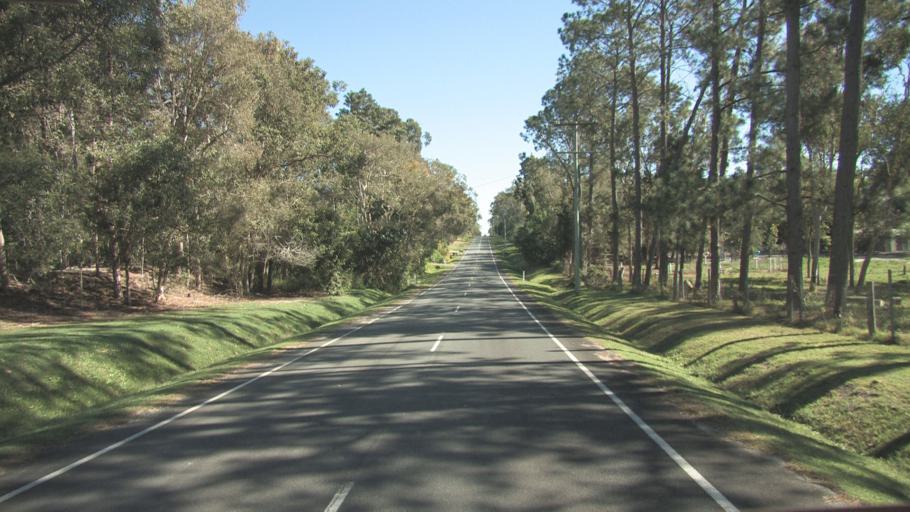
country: AU
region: Queensland
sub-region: Logan
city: Park Ridge South
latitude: -27.7074
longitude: 153.0484
